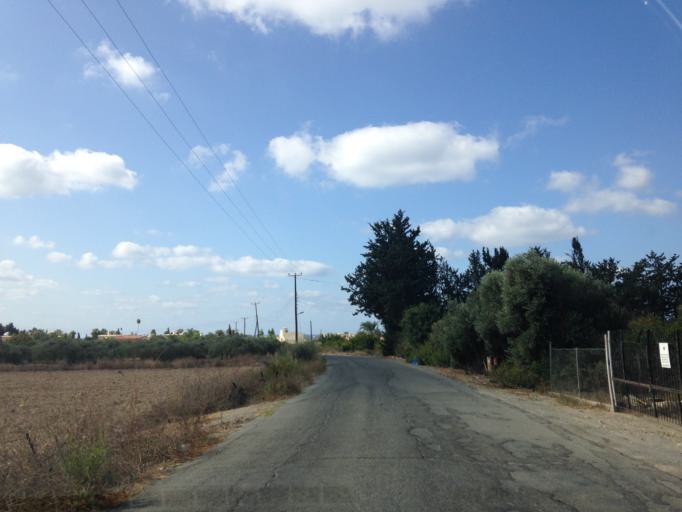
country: CY
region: Pafos
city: Pegeia
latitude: 34.8648
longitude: 32.3594
